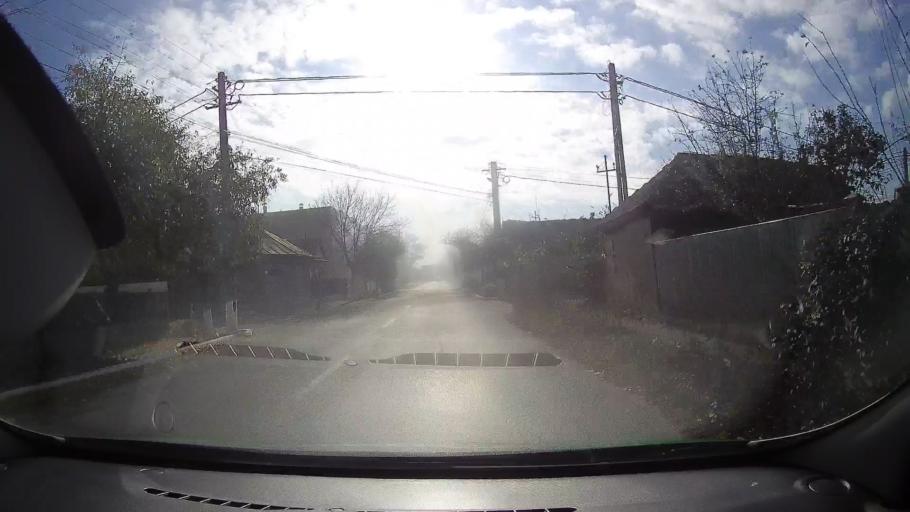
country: RO
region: Tulcea
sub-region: Comuna Sarichioi
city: Sarichioi
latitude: 44.9461
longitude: 28.8530
